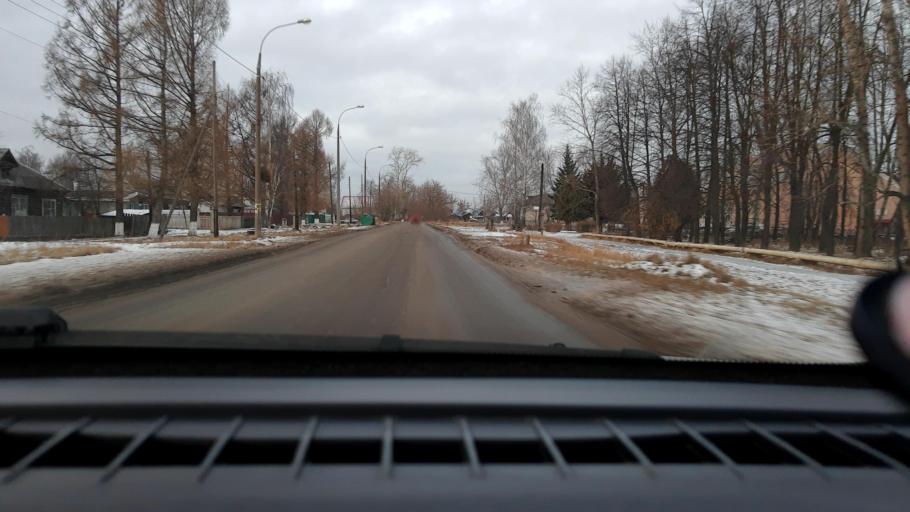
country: RU
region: Nizjnij Novgorod
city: Gorbatovka
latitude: 56.2470
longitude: 43.7481
